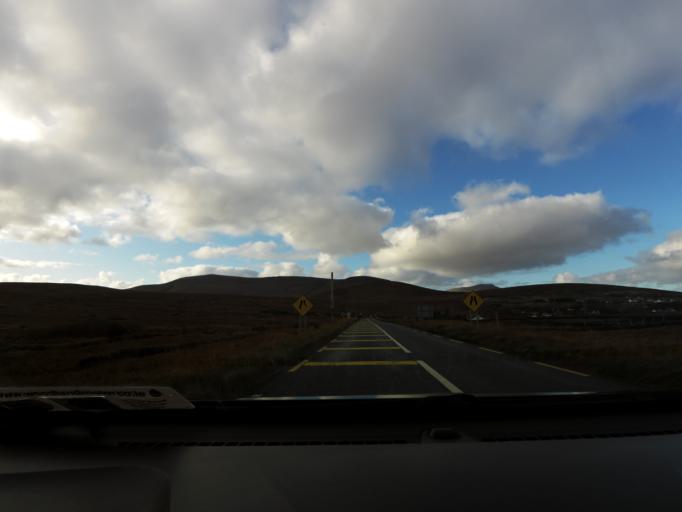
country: IE
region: Connaught
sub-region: Maigh Eo
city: Belmullet
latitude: 53.9443
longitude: -9.9707
